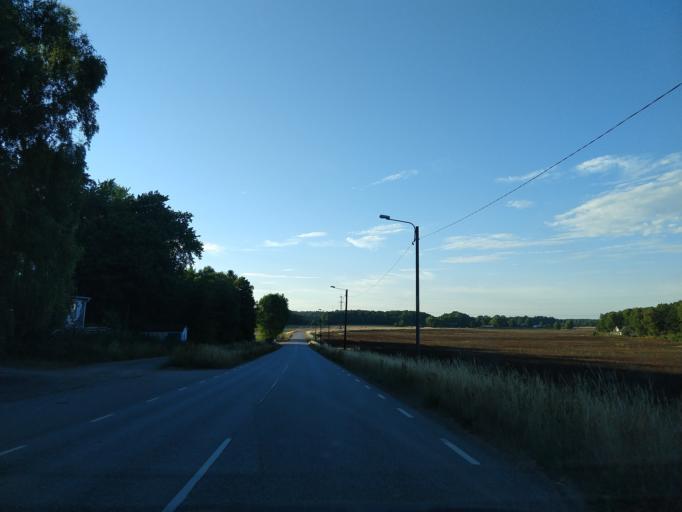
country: SE
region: Blekinge
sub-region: Ronneby Kommun
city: Brakne-Hoby
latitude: 56.2435
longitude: 15.1177
